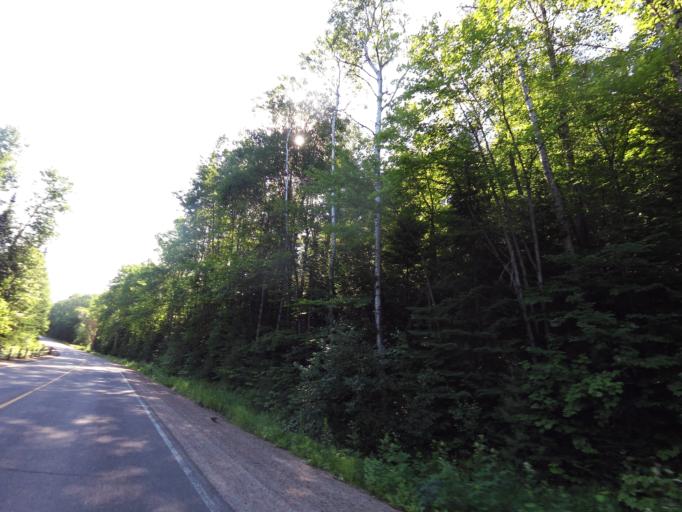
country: CA
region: Ontario
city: Deep River
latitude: 46.1790
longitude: -77.6855
